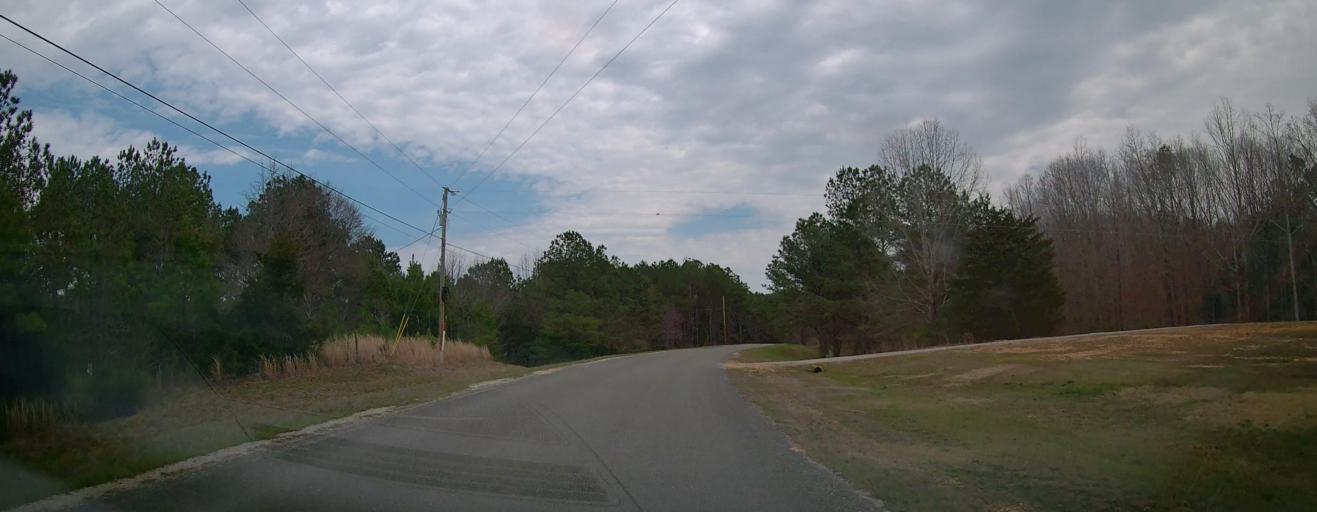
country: US
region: Mississippi
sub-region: Itawamba County
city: Fulton
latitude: 34.2140
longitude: -88.2034
